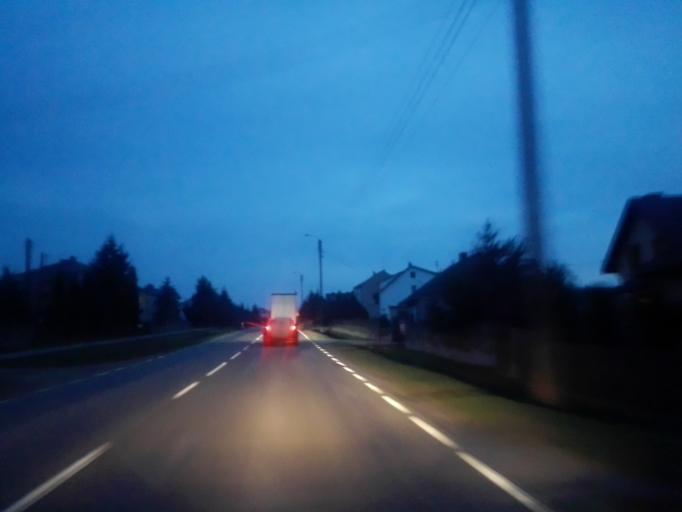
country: PL
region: Podlasie
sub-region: Lomza
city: Lomza
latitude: 53.1314
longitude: 22.0405
